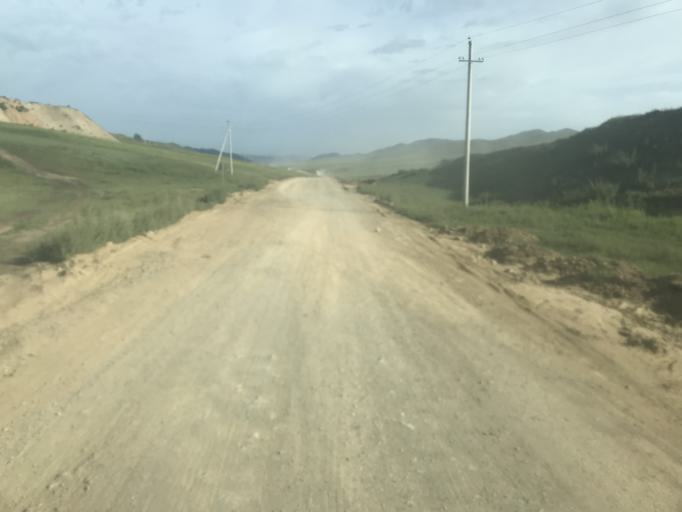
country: MN
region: Central Aimak
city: Javhlant
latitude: 48.7310
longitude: 106.1340
